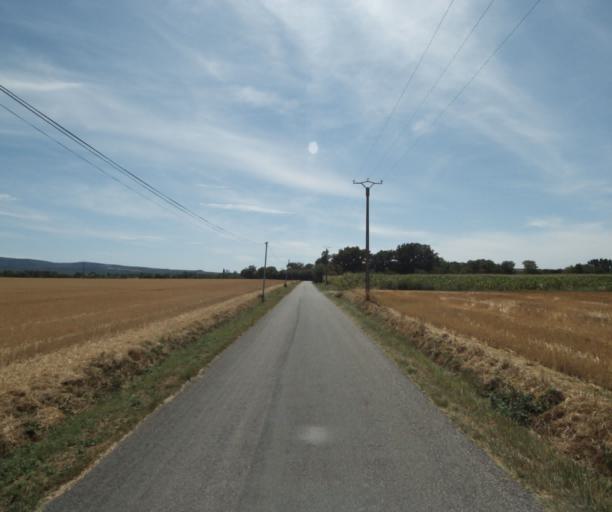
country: FR
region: Midi-Pyrenees
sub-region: Departement de la Haute-Garonne
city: Revel
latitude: 43.4992
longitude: 2.0234
